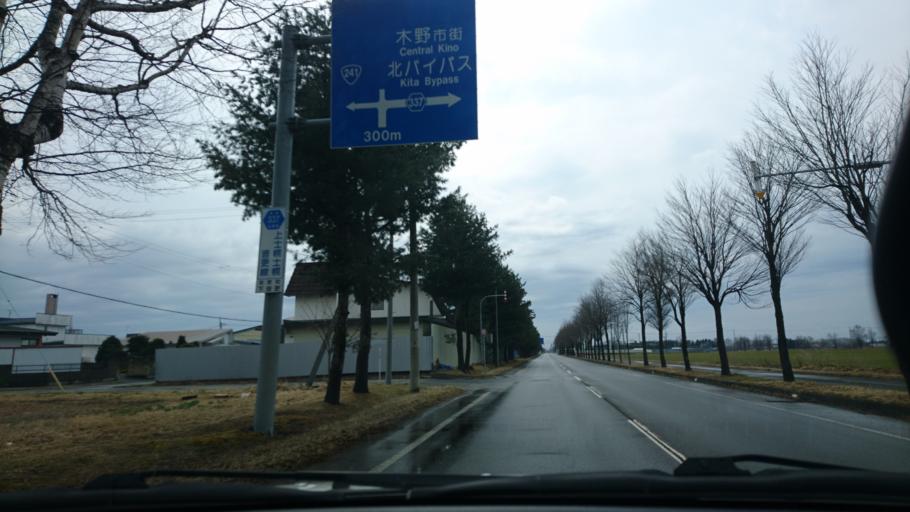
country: JP
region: Hokkaido
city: Otofuke
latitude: 42.9743
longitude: 143.1916
